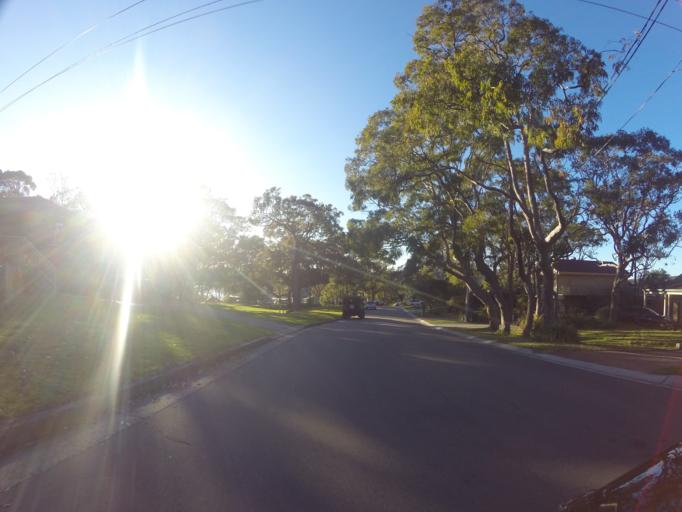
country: AU
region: New South Wales
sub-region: Sutherland Shire
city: Grays Point
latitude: -34.0604
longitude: 151.0875
